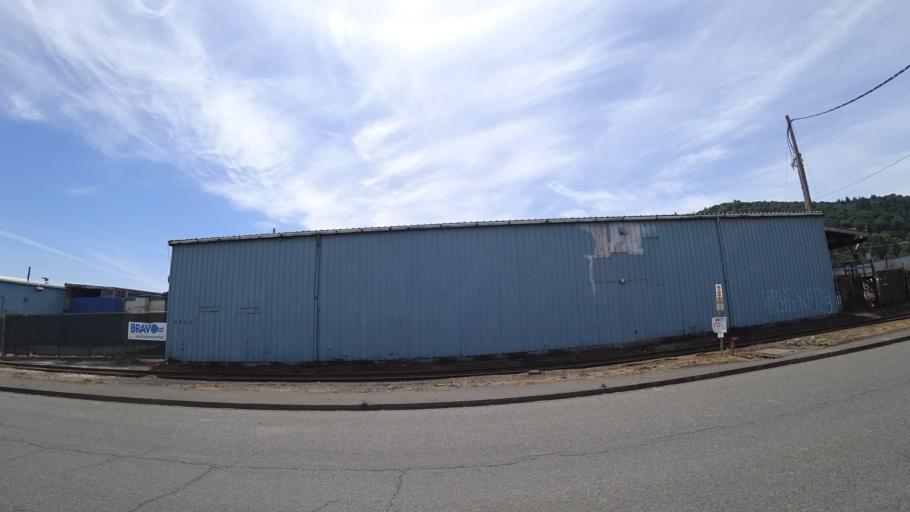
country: US
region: Oregon
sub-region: Washington County
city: West Haven
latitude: 45.5571
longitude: -122.7288
